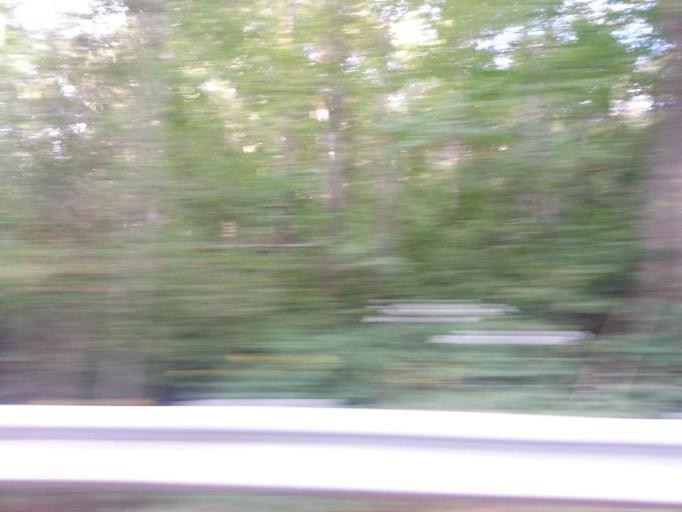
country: US
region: Tennessee
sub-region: Blount County
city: Wildwood
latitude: 35.8734
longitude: -83.8702
